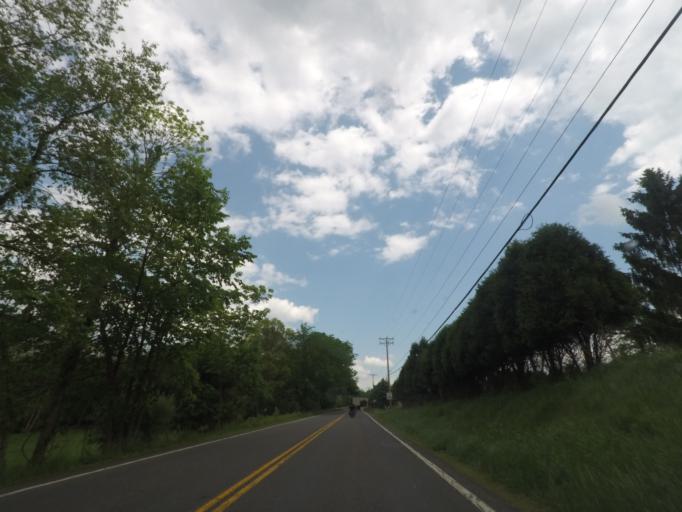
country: US
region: New York
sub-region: Dutchess County
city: Pine Plains
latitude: 42.0506
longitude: -73.6241
